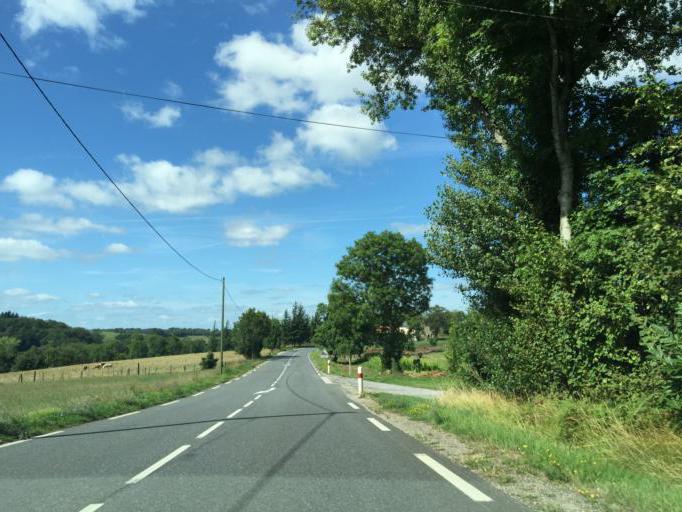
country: FR
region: Midi-Pyrenees
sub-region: Departement de l'Aveyron
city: Villefranche-de-Rouergue
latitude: 44.3334
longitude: 2.0675
